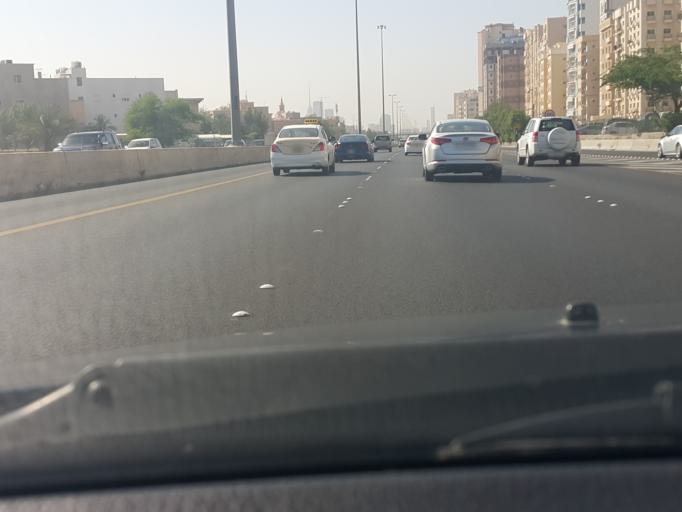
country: KW
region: Muhafazat Hawalli
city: Hawalli
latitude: 29.3257
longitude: 48.0103
